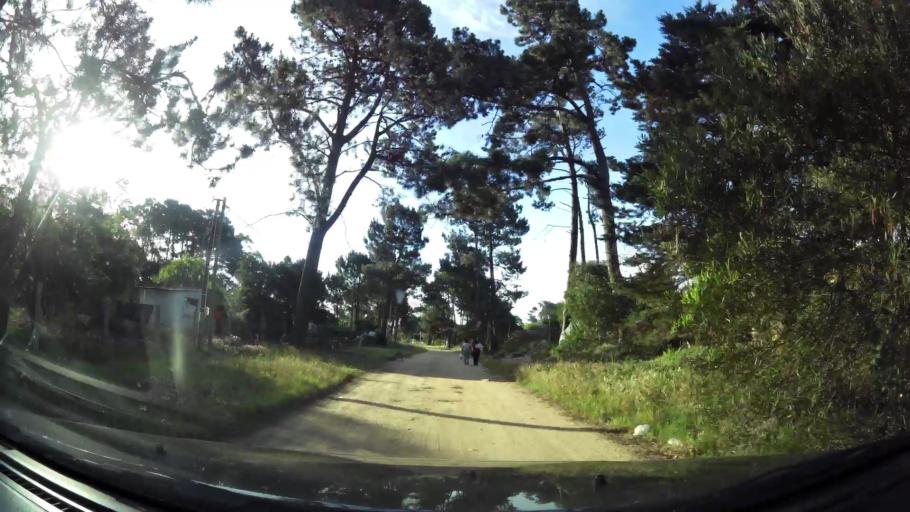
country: UY
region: Canelones
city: Empalme Olmos
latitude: -34.7724
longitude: -55.8578
